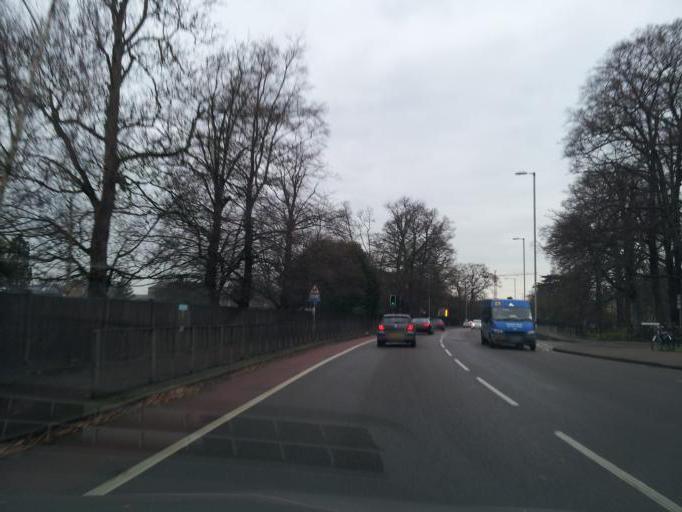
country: GB
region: England
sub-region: Cambridgeshire
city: Cambridge
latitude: 52.1946
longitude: 0.1225
